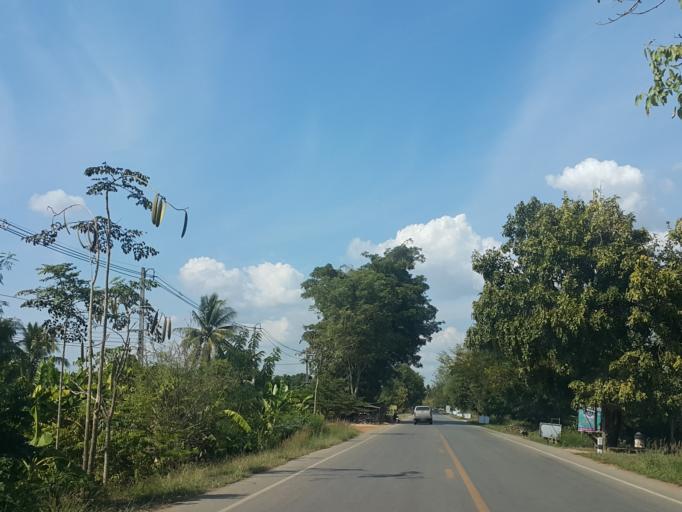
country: TH
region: Sukhothai
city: Sawankhalok
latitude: 17.2877
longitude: 99.8340
